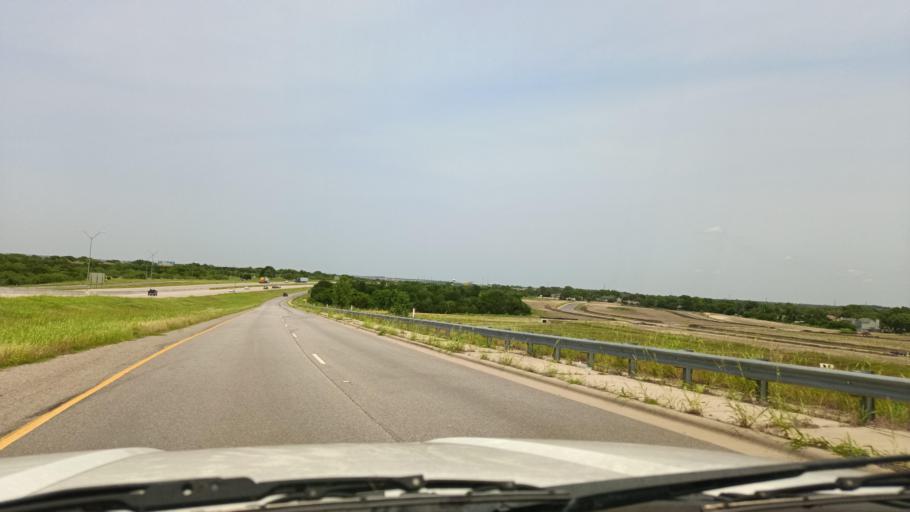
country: US
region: Texas
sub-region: Bell County
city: Temple
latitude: 31.0948
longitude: -97.3894
